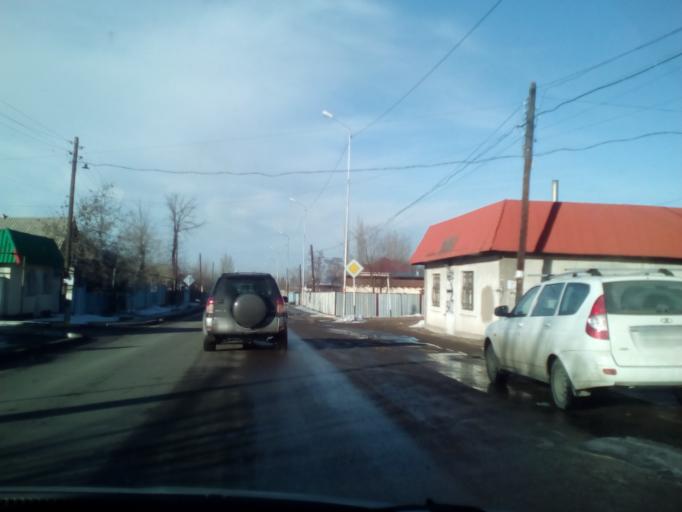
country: KZ
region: Almaty Oblysy
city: Burunday
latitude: 43.1725
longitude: 76.4157
